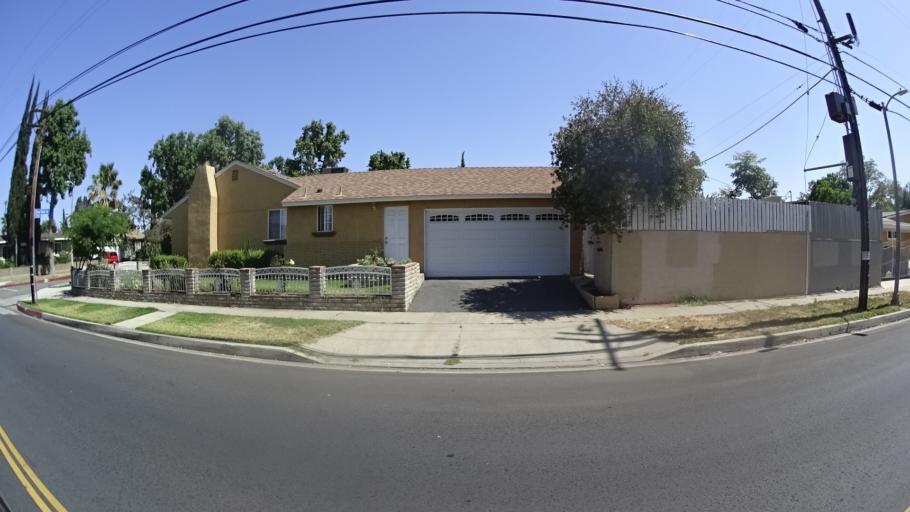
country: US
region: California
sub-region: Los Angeles County
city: Van Nuys
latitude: 34.2165
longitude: -118.4367
